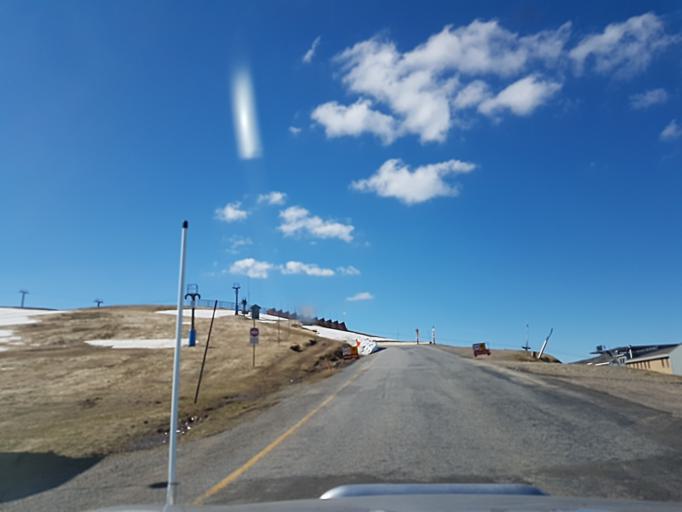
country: AU
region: Victoria
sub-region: Alpine
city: Mount Beauty
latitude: -36.9810
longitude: 147.1421
